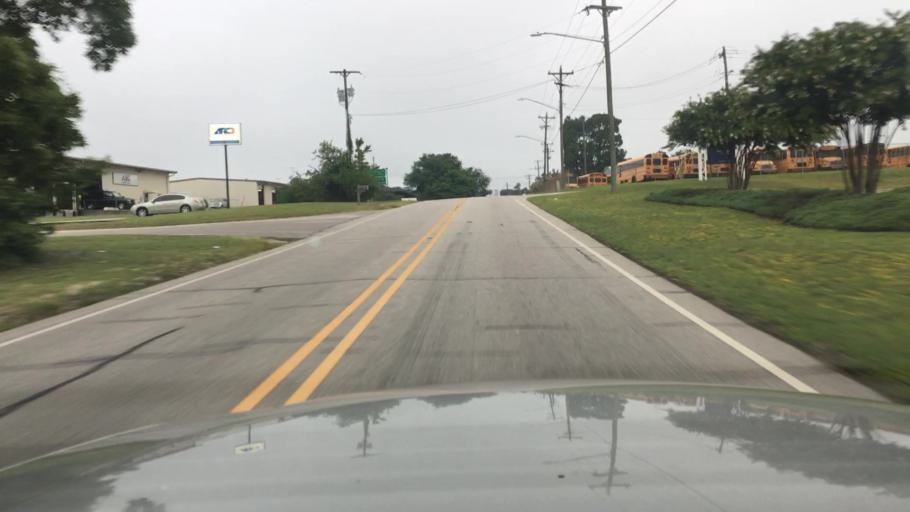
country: US
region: North Carolina
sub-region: Cumberland County
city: Fayetteville
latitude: 35.0125
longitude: -78.8933
